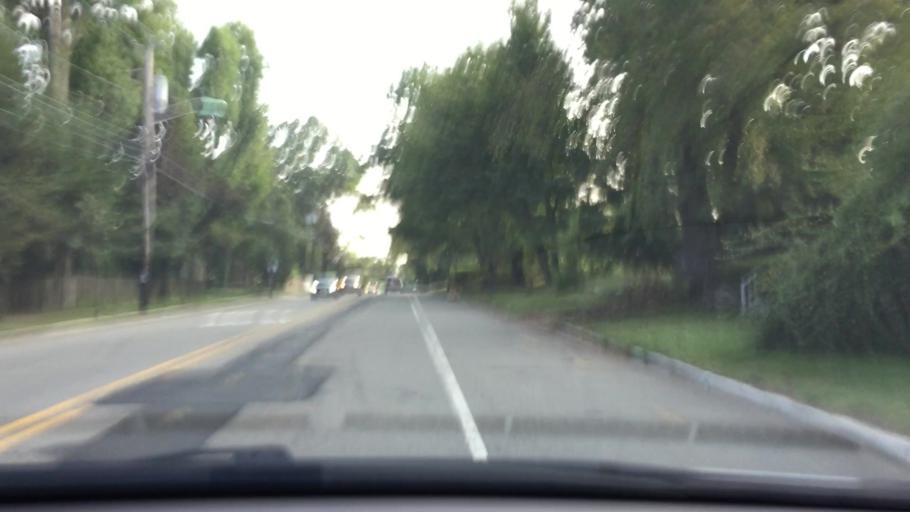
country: US
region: New Jersey
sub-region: Essex County
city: Upper Montclair
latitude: 40.8334
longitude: -74.1968
